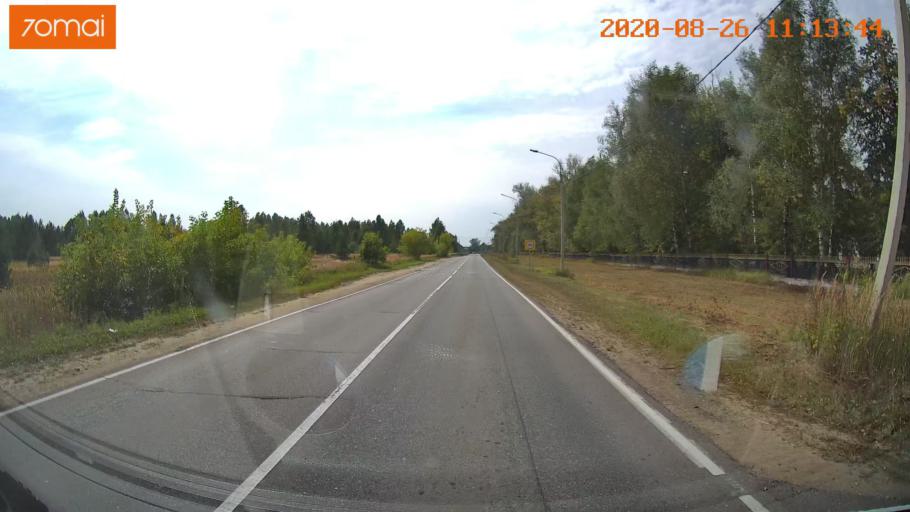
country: RU
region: Rjazan
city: Izhevskoye
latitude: 54.4539
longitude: 41.1190
